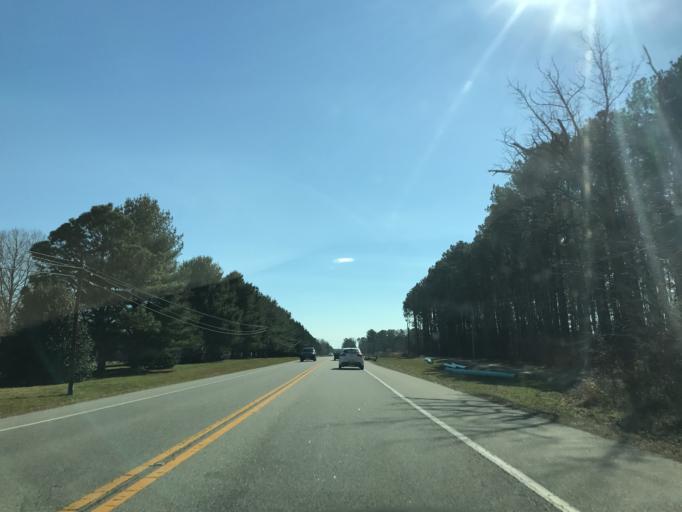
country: US
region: Maryland
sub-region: Queen Anne's County
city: Stevensville
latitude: 38.9224
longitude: -76.3550
